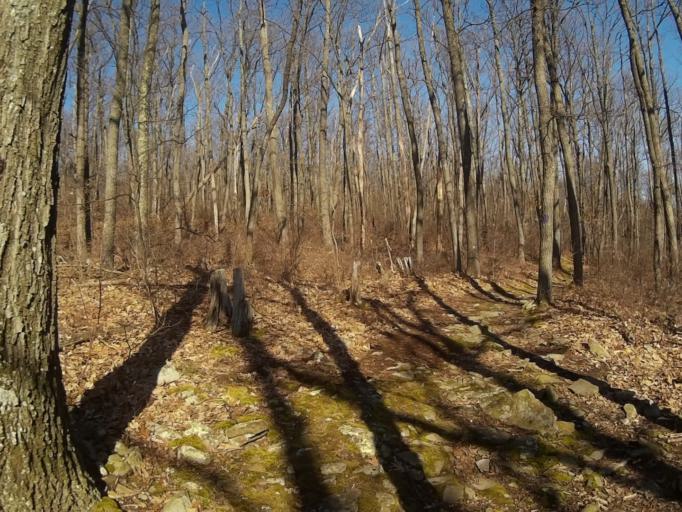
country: US
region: Pennsylvania
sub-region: Centre County
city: Lemont
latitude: 40.8073
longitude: -77.7965
